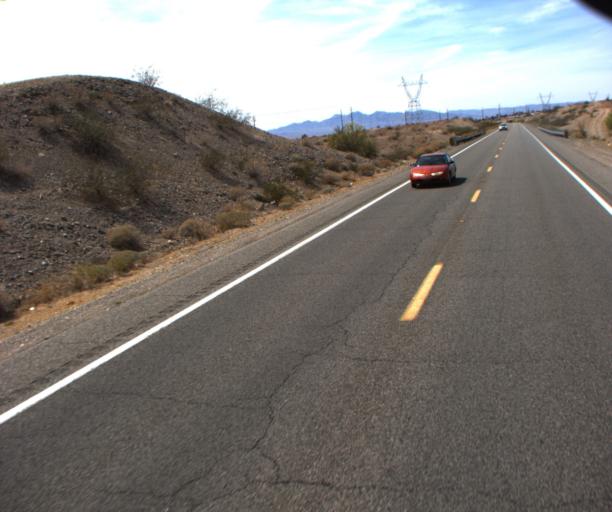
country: US
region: Arizona
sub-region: Mohave County
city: Lake Havasu City
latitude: 34.4459
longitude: -114.2378
